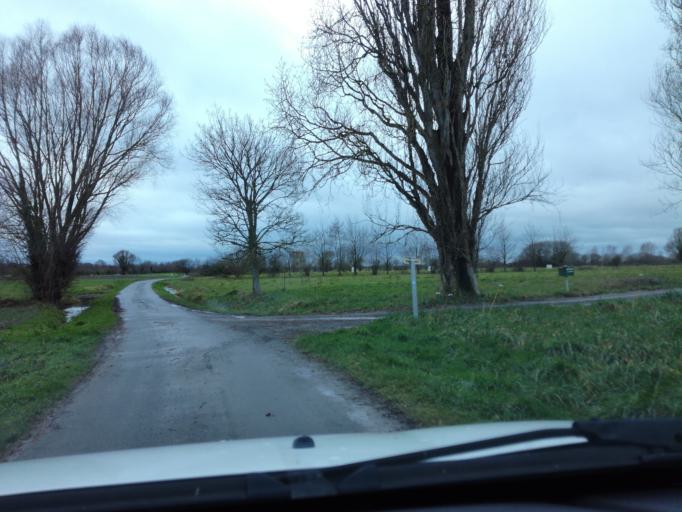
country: FR
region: Brittany
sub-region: Departement d'Ille-et-Vilaine
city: Baguer-Pican
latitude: 48.5748
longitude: -1.7009
